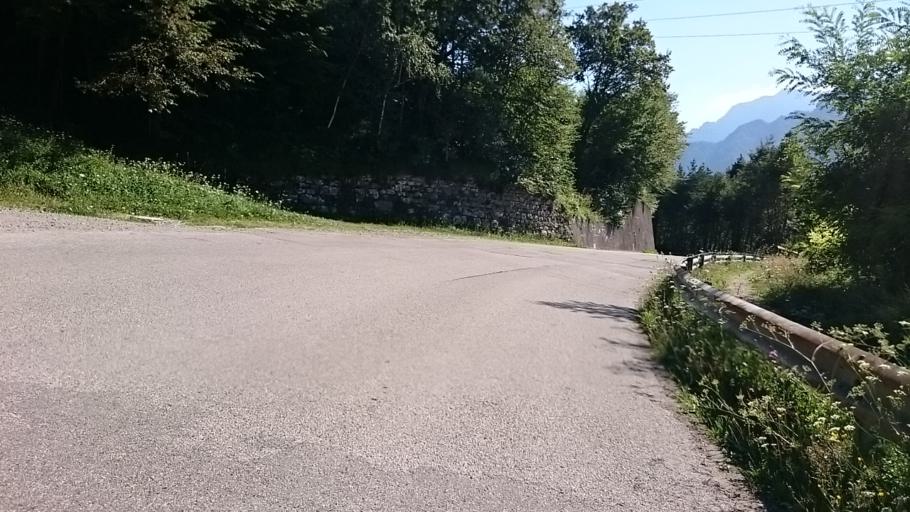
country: IT
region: Veneto
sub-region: Provincia di Belluno
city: Longarone
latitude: 46.2505
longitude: 12.3139
